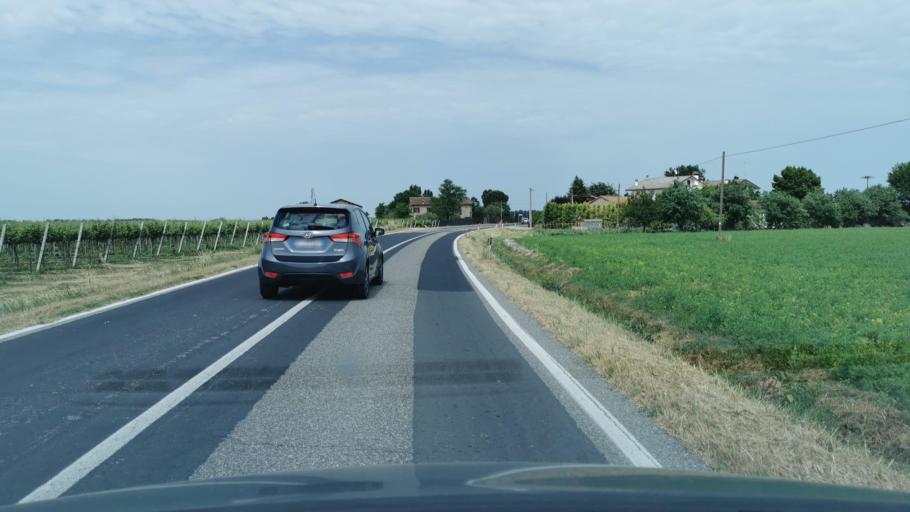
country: IT
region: Emilia-Romagna
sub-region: Provincia di Ravenna
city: Glorie
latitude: 44.4927
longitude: 12.0751
